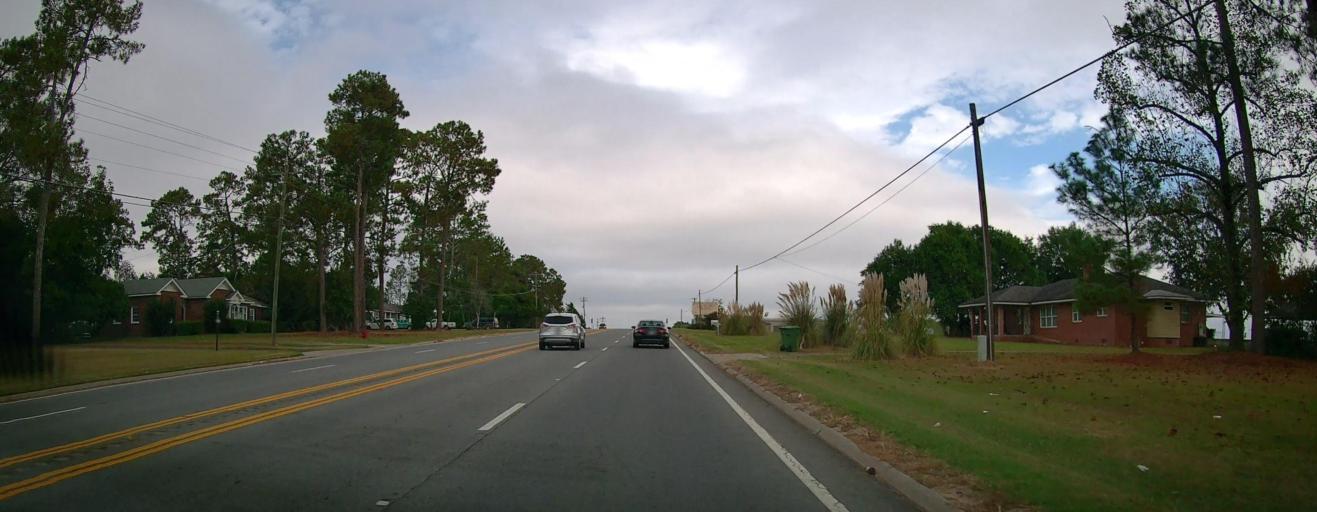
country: US
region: Georgia
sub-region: Tift County
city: Omega
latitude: 31.3445
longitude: -83.5900
